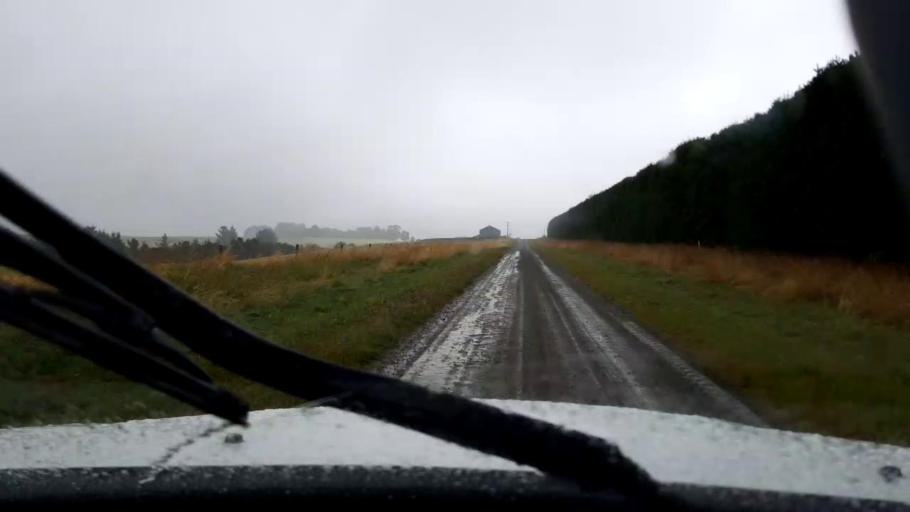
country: NZ
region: Canterbury
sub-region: Timaru District
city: Pleasant Point
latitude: -44.1697
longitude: 171.1487
